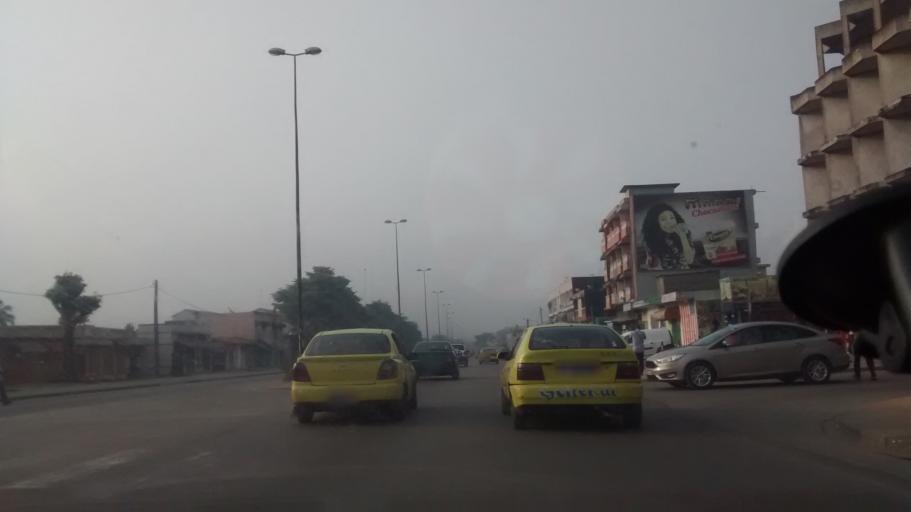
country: CI
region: Lagunes
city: Abobo
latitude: 5.4016
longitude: -3.9912
